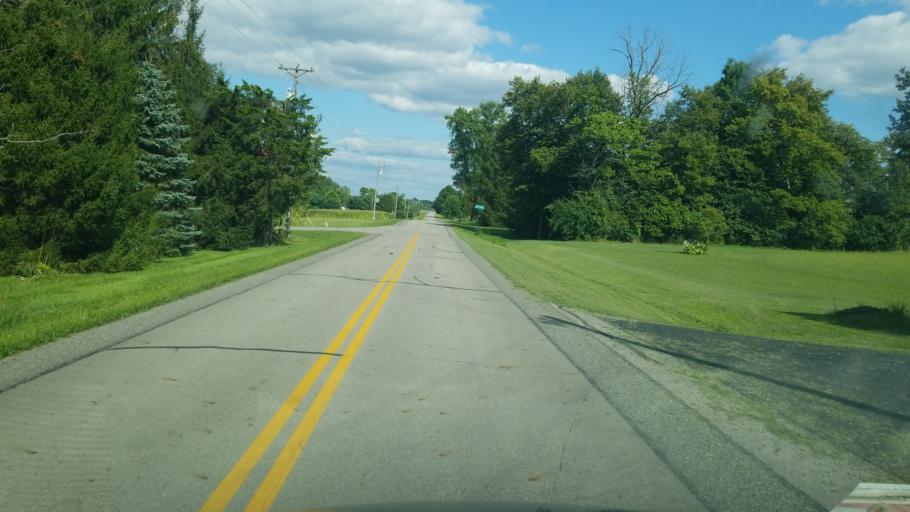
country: US
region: Ohio
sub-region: Champaign County
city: Saint Paris
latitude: 40.1560
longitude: -83.8778
